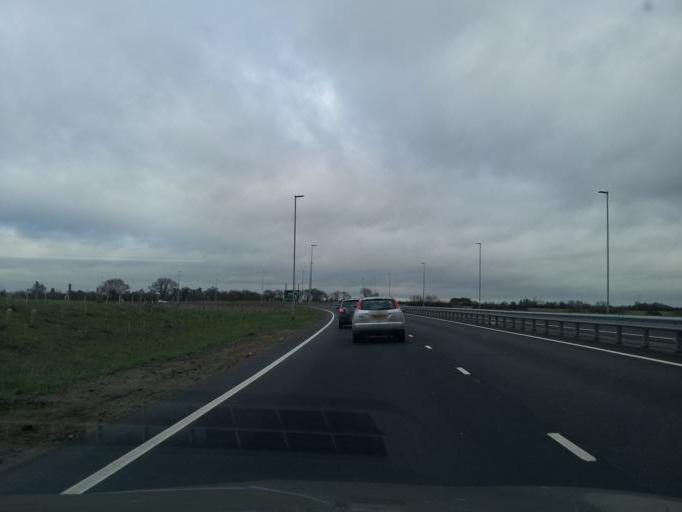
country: GB
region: England
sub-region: Norfolk
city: Surlingham
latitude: 52.6294
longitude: 1.3862
